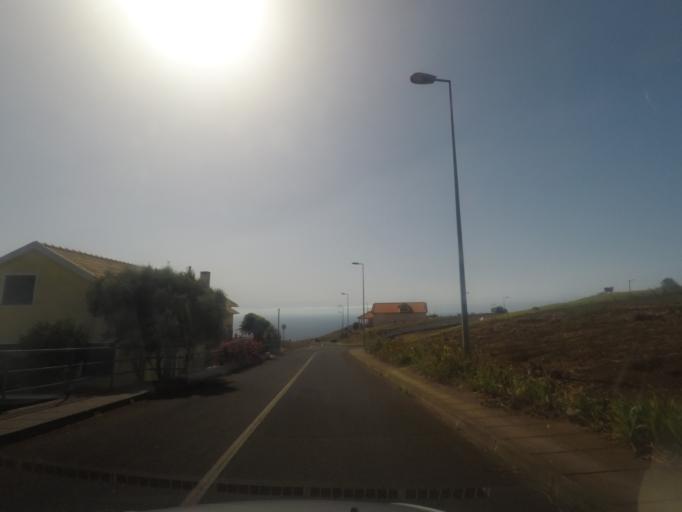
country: PT
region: Madeira
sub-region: Calheta
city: Faja da Ovelha
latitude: 32.8140
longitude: -17.2513
